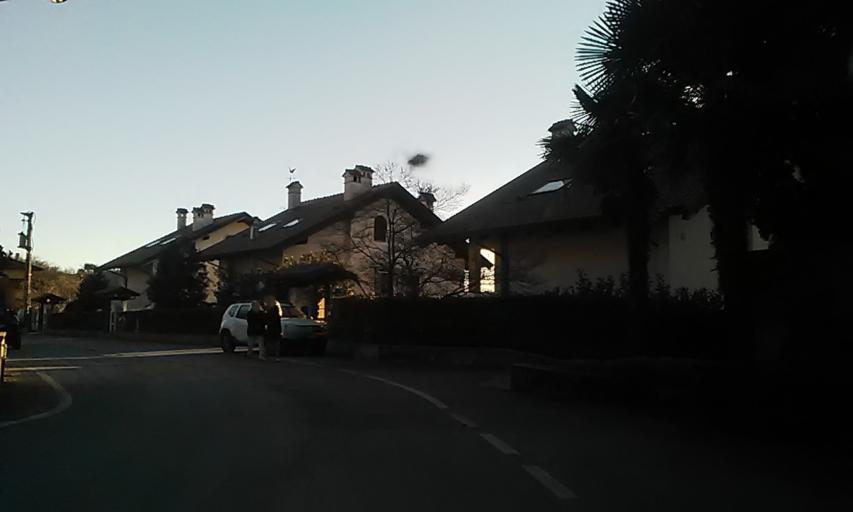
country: IT
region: Piedmont
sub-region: Provincia di Vercelli
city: Borgosesia
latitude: 45.7308
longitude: 8.2678
